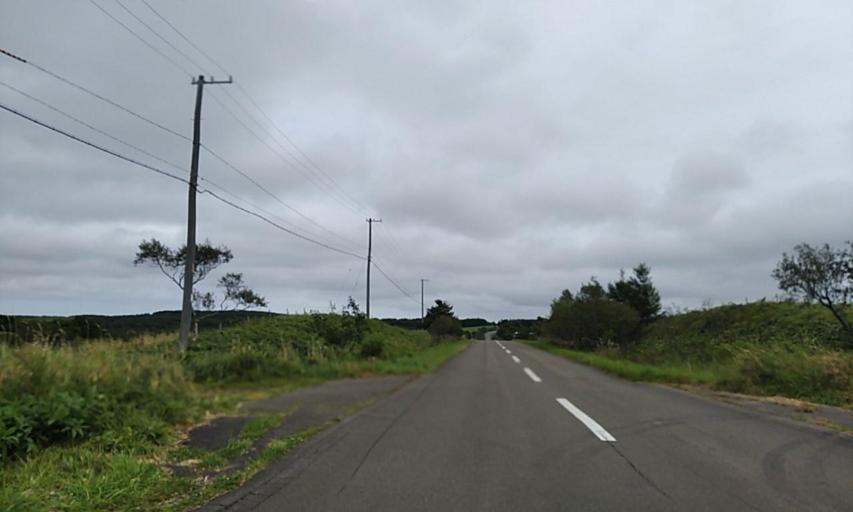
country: JP
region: Hokkaido
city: Nemuro
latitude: 43.2706
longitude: 145.2719
